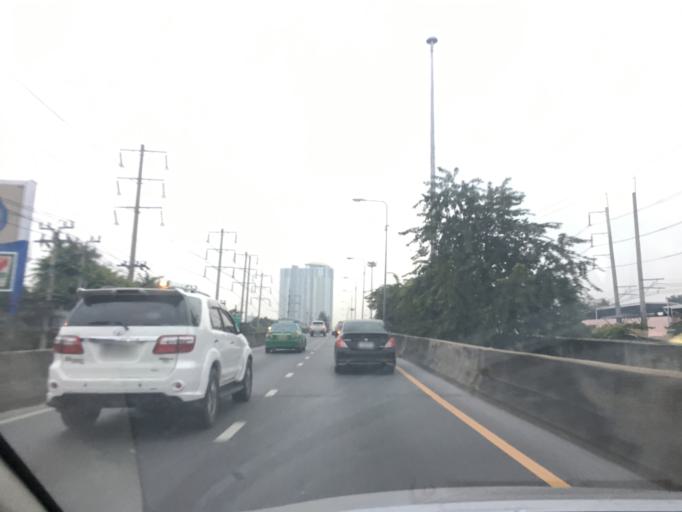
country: TH
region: Bangkok
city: Yan Nawa
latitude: 13.6972
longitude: 100.5464
